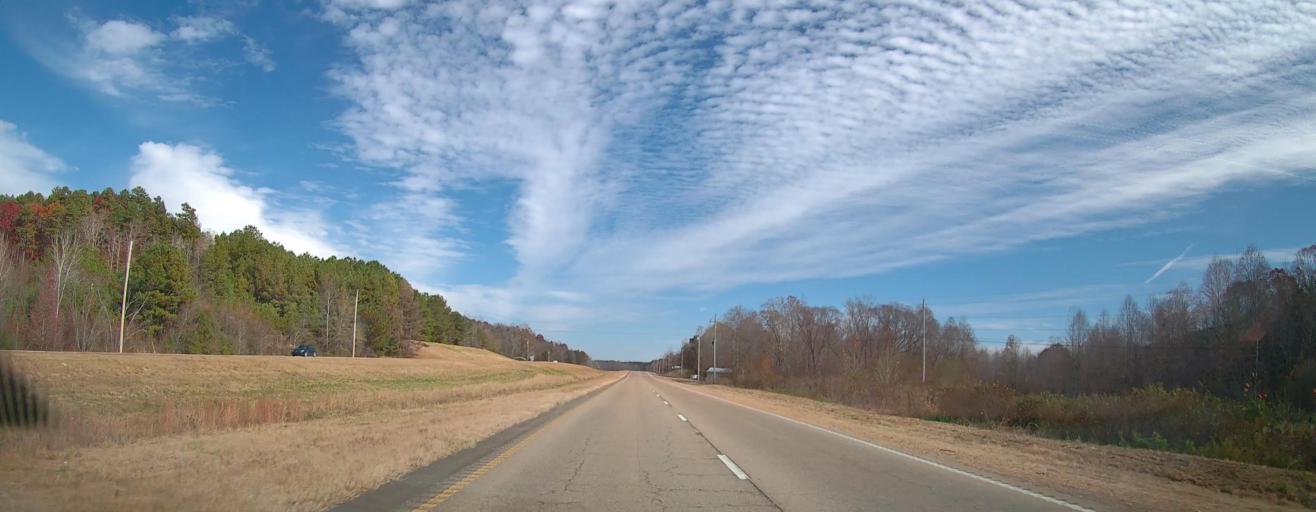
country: US
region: Mississippi
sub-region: Alcorn County
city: Corinth
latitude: 34.9330
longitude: -88.7525
